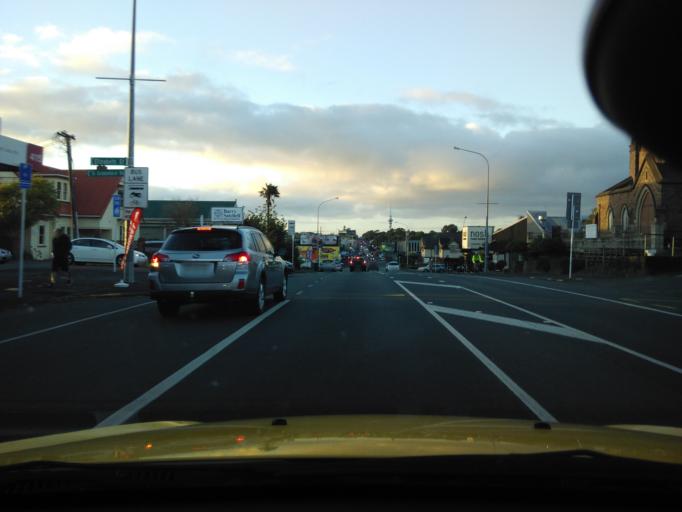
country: NZ
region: Auckland
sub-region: Auckland
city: Auckland
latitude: -36.8823
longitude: 174.7491
